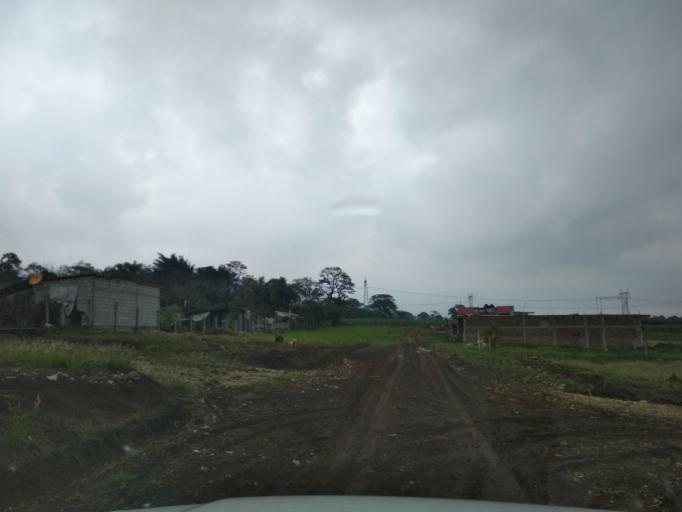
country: MX
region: Veracruz
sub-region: Cordoba
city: Veinte de Noviembre
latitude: 18.8609
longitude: -96.9654
